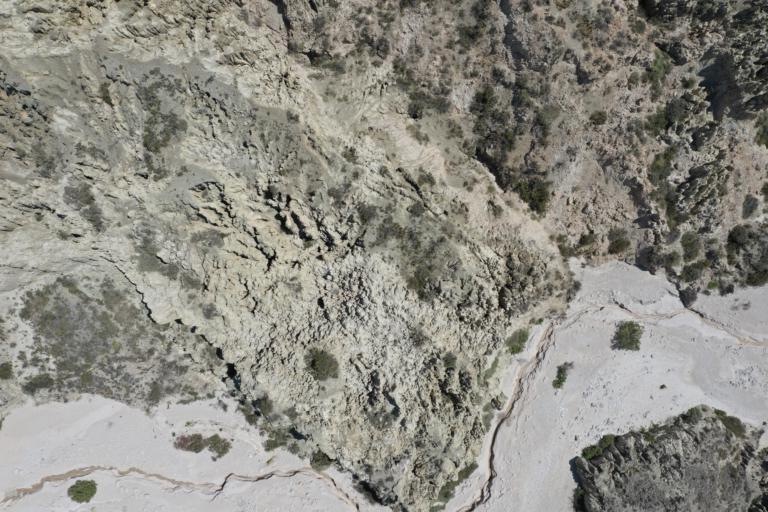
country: BO
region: La Paz
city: La Paz
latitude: -16.5623
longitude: -68.1143
